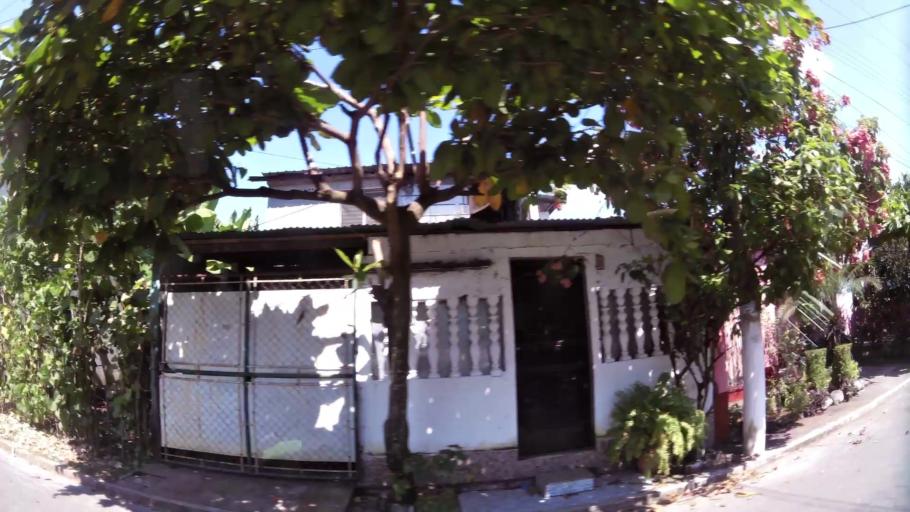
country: GT
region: Suchitepeque
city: Mazatenango
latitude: 14.5355
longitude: -91.4840
